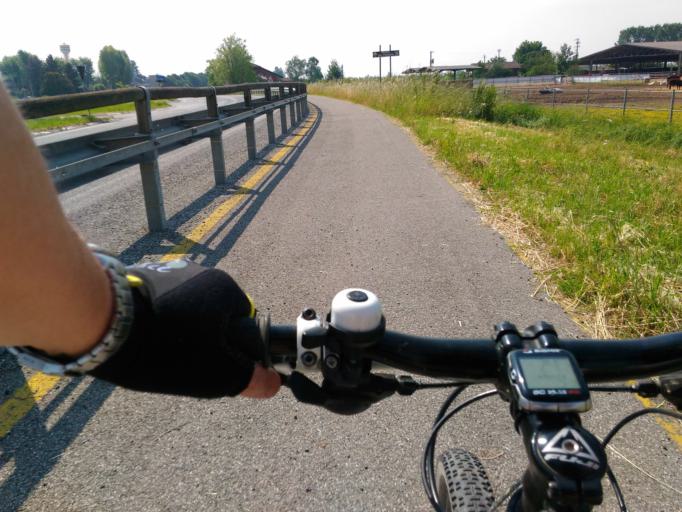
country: IT
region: Lombardy
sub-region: Provincia di Lodi
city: Salerano sul Lambro
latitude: 45.2920
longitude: 9.3752
